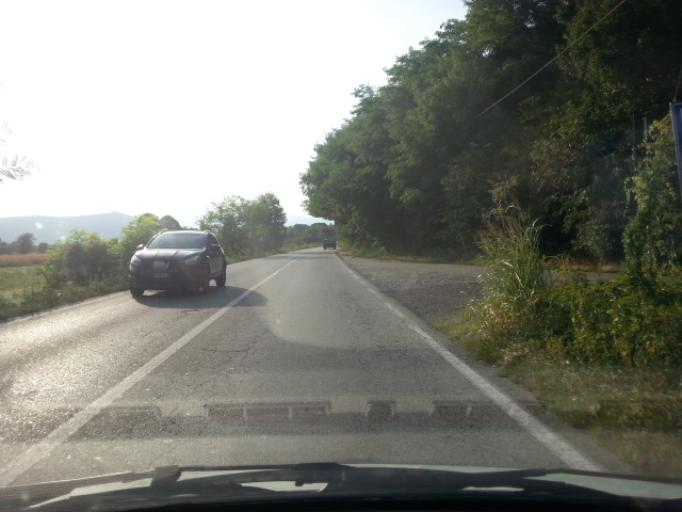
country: IT
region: Piedmont
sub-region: Provincia di Torino
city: Rivalta di Torino
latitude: 45.0285
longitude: 7.5399
